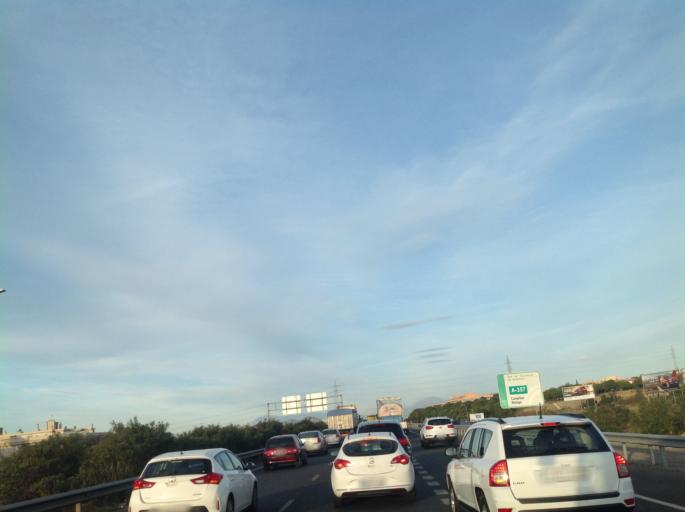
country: ES
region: Andalusia
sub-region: Provincia de Malaga
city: Malaga
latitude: 36.7126
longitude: -4.4623
